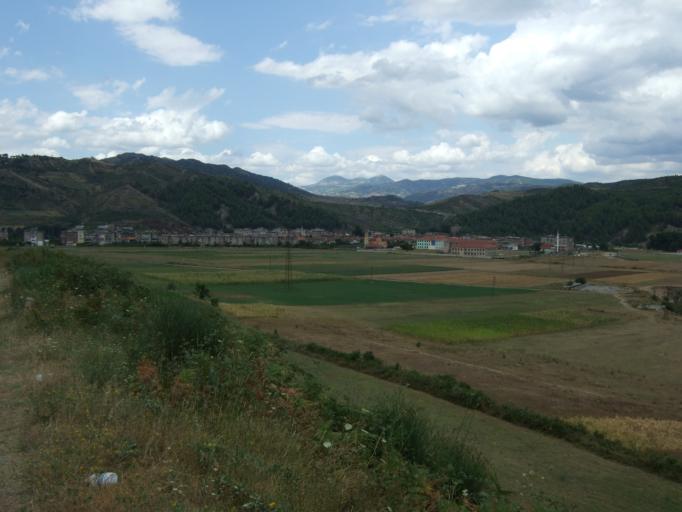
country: AL
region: Gjirokaster
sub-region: Rrethi i Tepelenes
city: Memaliaj
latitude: 40.3428
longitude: 19.9823
